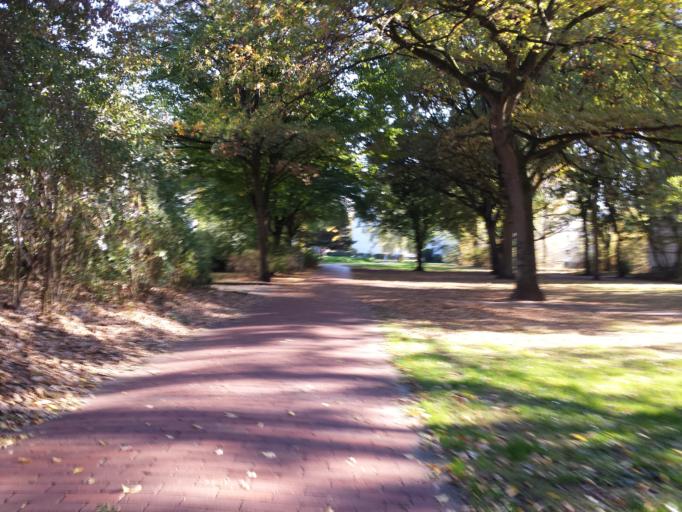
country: DE
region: Bremen
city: Bremen
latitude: 53.0894
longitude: 8.7893
